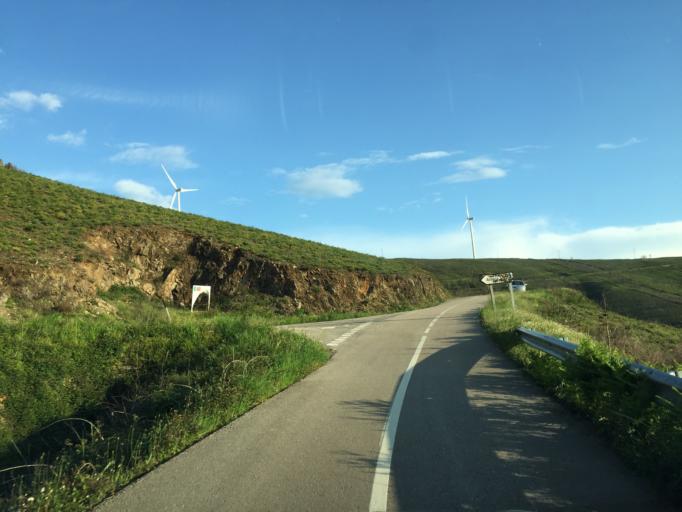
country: PT
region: Coimbra
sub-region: Pampilhosa da Serra
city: Pampilhosa da Serra
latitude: 40.1211
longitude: -8.0119
